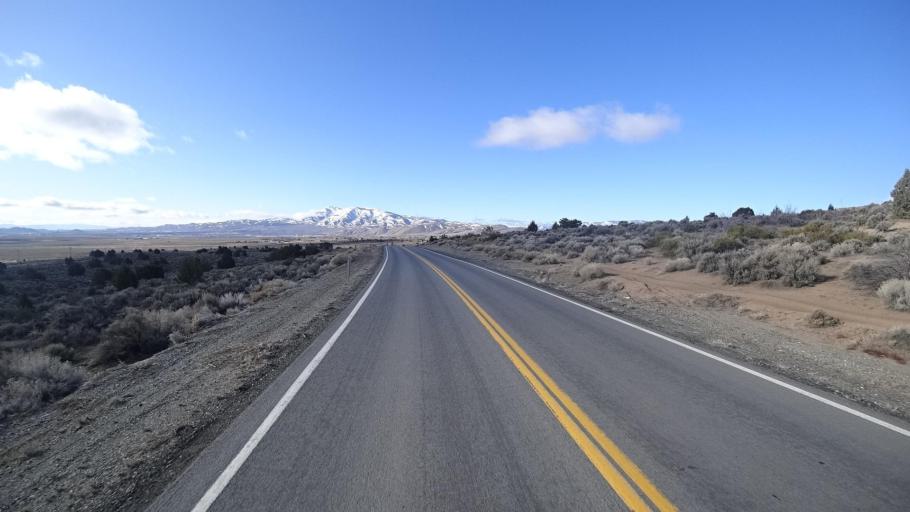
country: US
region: Nevada
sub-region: Washoe County
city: Cold Springs
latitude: 39.7068
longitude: -119.9061
